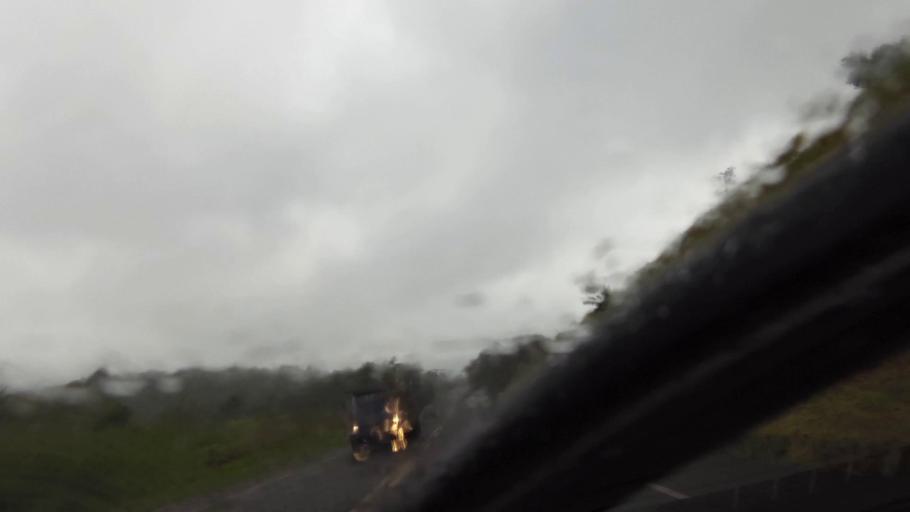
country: BR
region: Espirito Santo
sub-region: Guarapari
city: Guarapari
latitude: -20.6373
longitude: -40.5289
